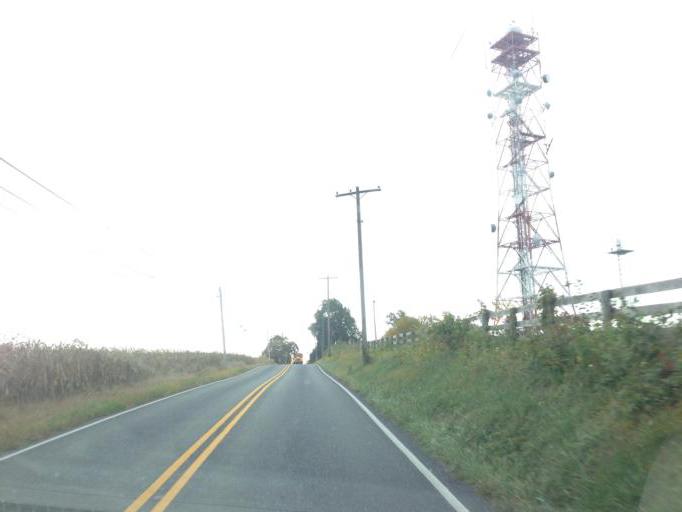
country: US
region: Maryland
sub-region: Carroll County
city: Mount Airy
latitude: 39.3486
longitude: -77.1716
